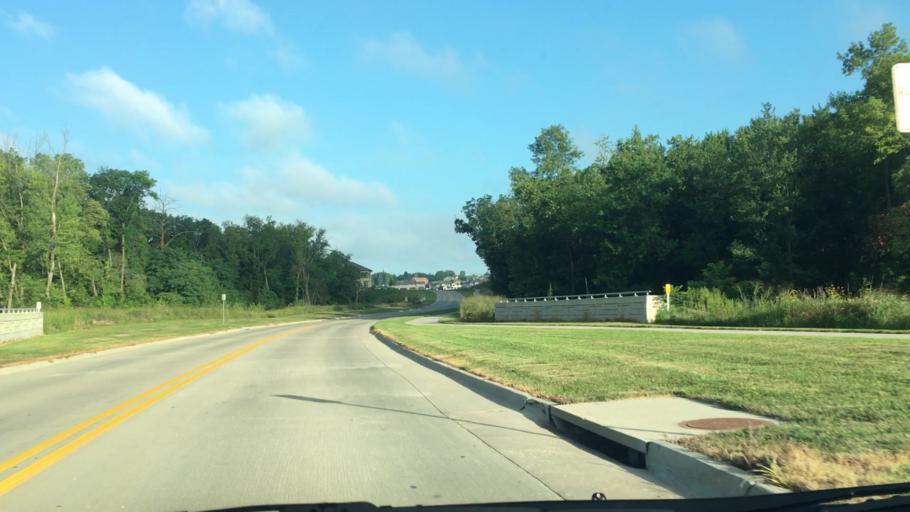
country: US
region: Iowa
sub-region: Johnson County
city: Coralville
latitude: 41.6996
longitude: -91.5490
